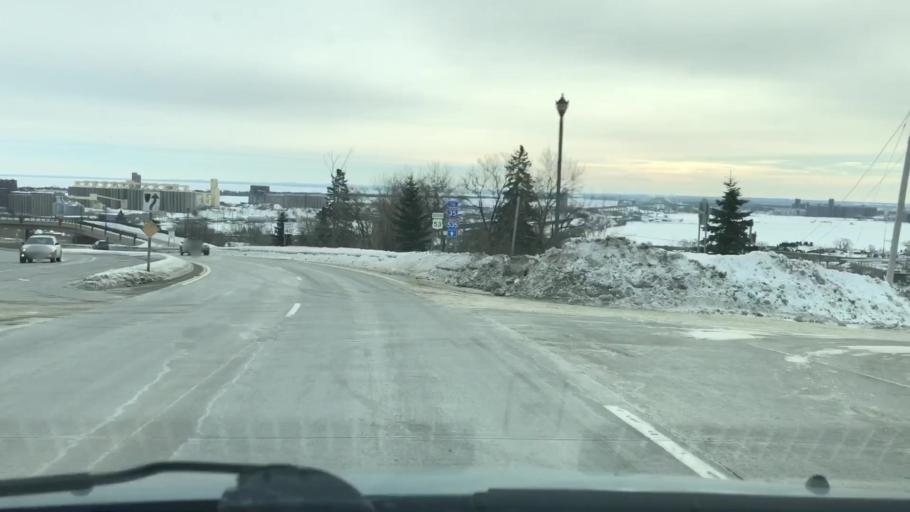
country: US
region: Minnesota
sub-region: Saint Louis County
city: Duluth
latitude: 46.7707
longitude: -92.1302
